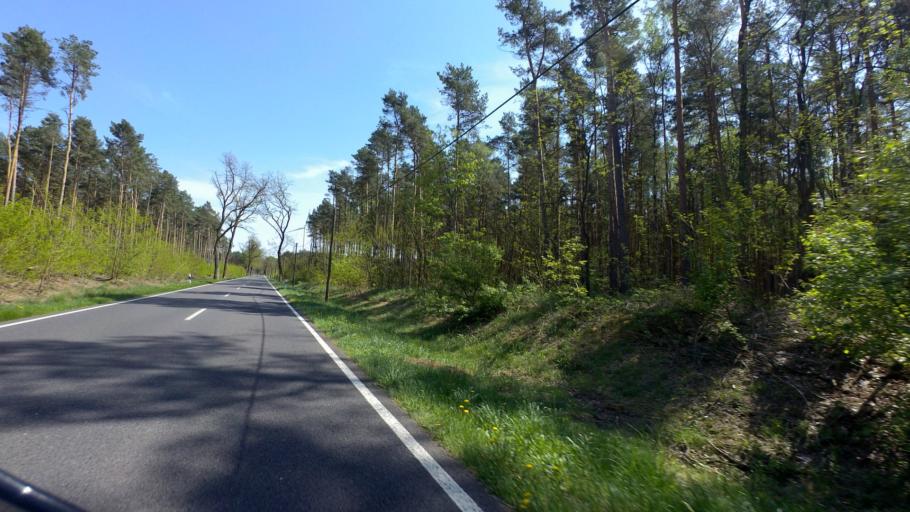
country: DE
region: Brandenburg
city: Neu Zauche
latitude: 51.9965
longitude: 14.0847
